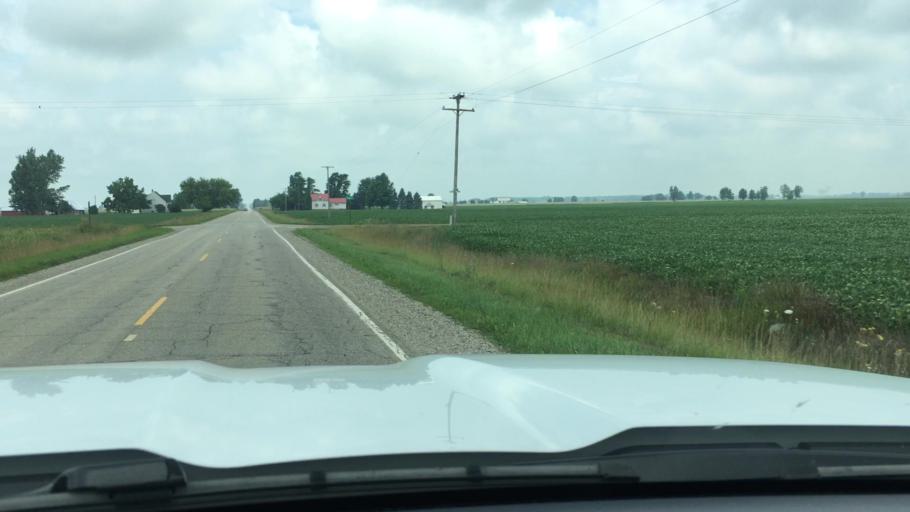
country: US
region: Michigan
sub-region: Sanilac County
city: Marlette
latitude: 43.3725
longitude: -83.0062
